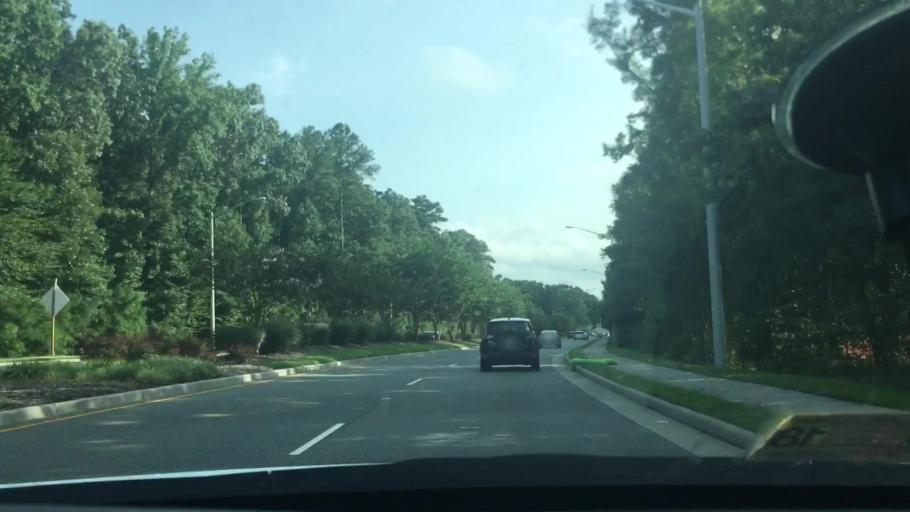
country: US
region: Virginia
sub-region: City of Virginia Beach
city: Virginia Beach
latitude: 36.8277
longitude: -75.9973
